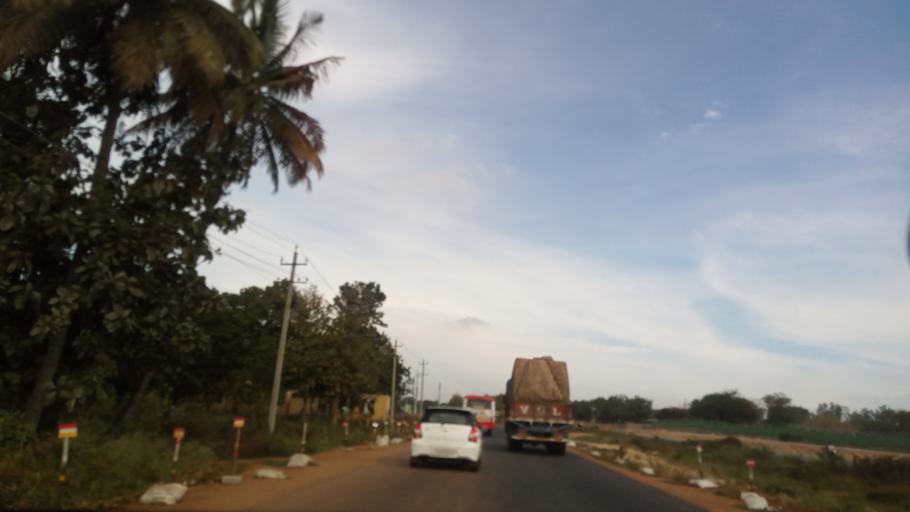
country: IN
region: Karnataka
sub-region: Mandya
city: Shrirangapattana
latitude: 12.4416
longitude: 76.7270
